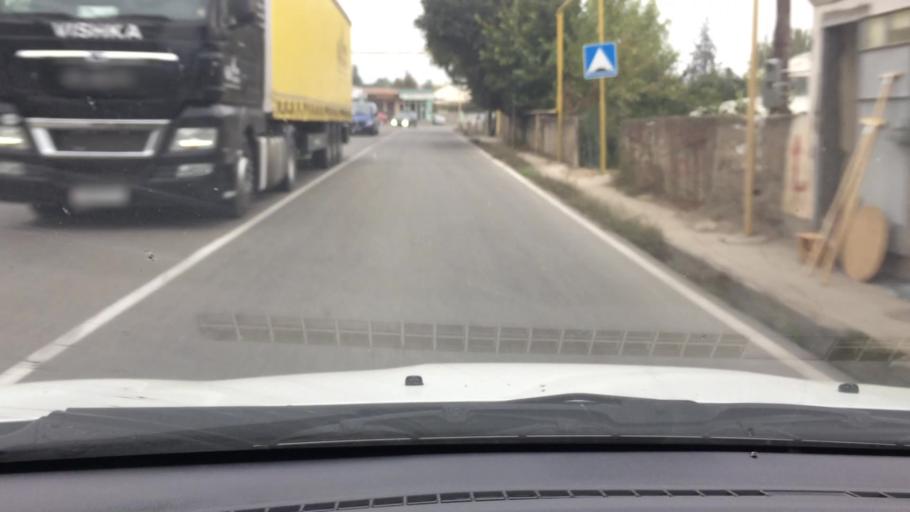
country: AM
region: Tavush
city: Bagratashen
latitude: 41.2444
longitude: 44.7979
